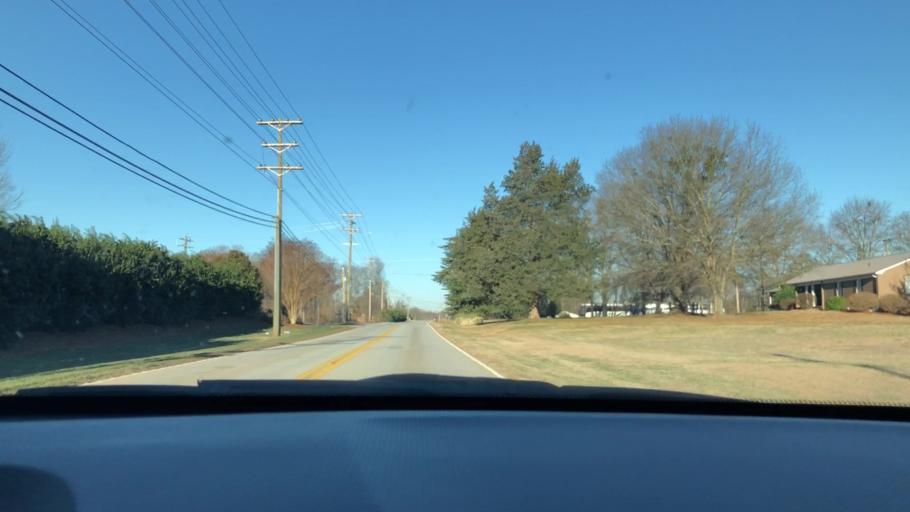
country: US
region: South Carolina
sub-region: Greenville County
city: Five Forks
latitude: 34.8195
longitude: -82.2078
